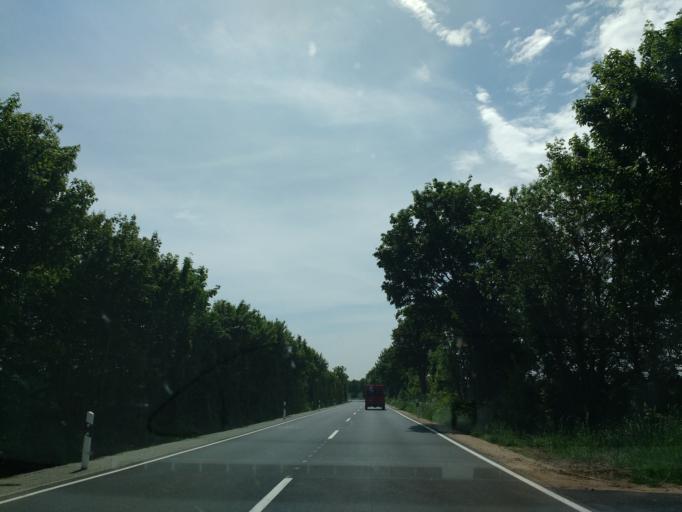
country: DE
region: Schleswig-Holstein
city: Braak
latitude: 53.6065
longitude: 10.2413
